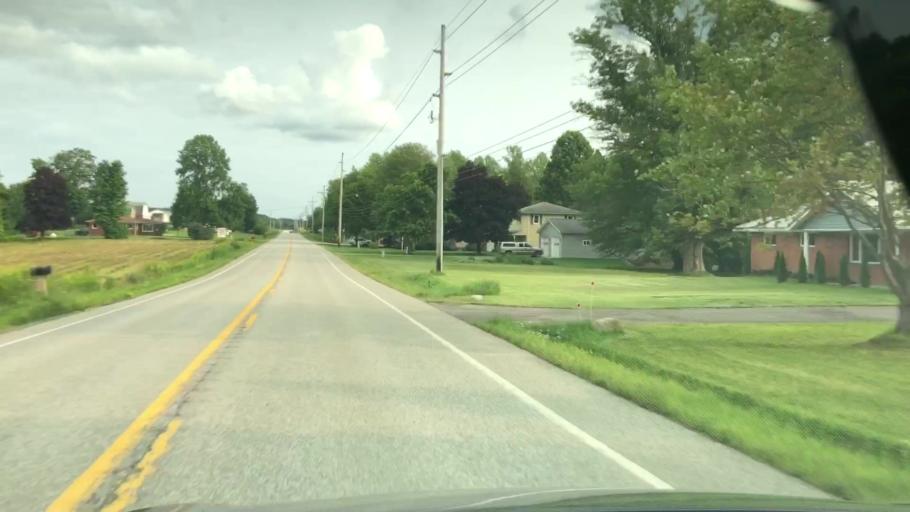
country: US
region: Pennsylvania
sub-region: Erie County
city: Union City
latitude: 41.9514
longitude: -79.8501
